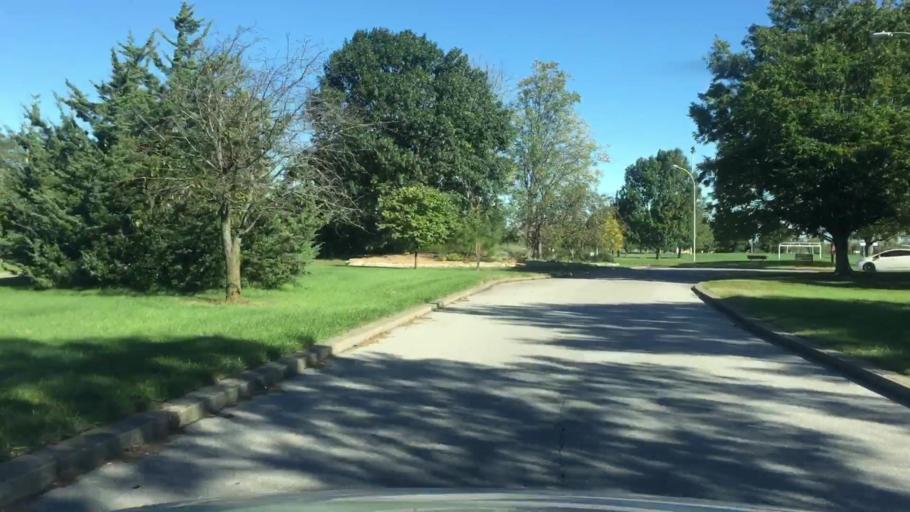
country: US
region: Missouri
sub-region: Boone County
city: Columbia
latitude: 38.9692
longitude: -92.3631
